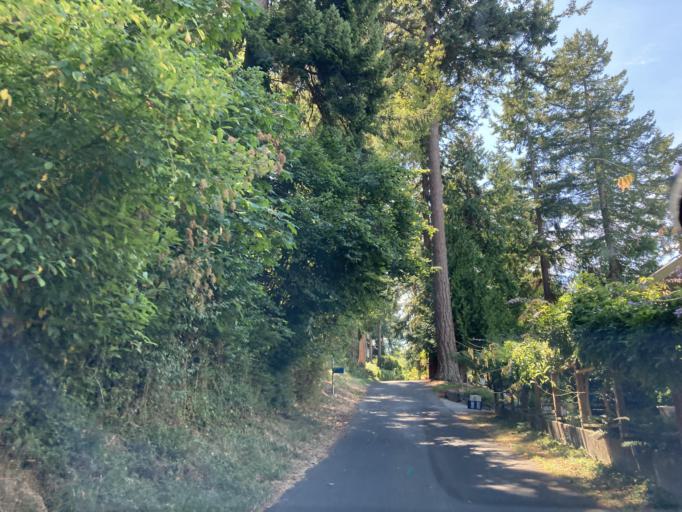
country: US
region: Washington
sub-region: Whatcom County
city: Bellingham
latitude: 48.7343
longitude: -122.4930
